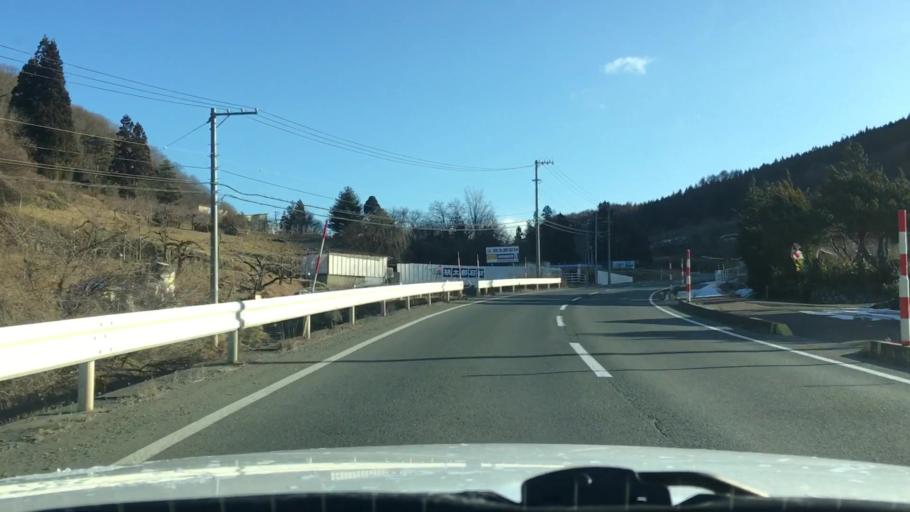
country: JP
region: Iwate
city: Morioka-shi
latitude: 39.6569
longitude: 141.1883
